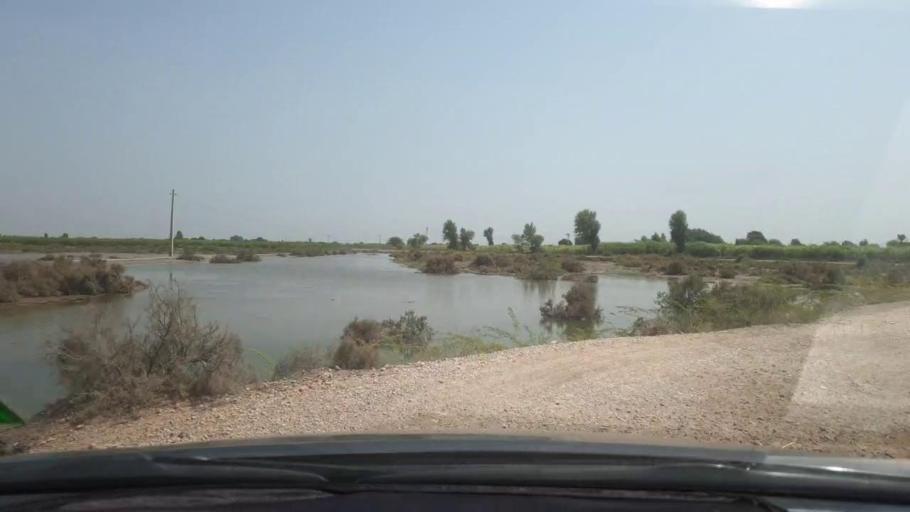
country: PK
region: Sindh
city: Tando Bago
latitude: 24.7832
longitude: 69.1787
